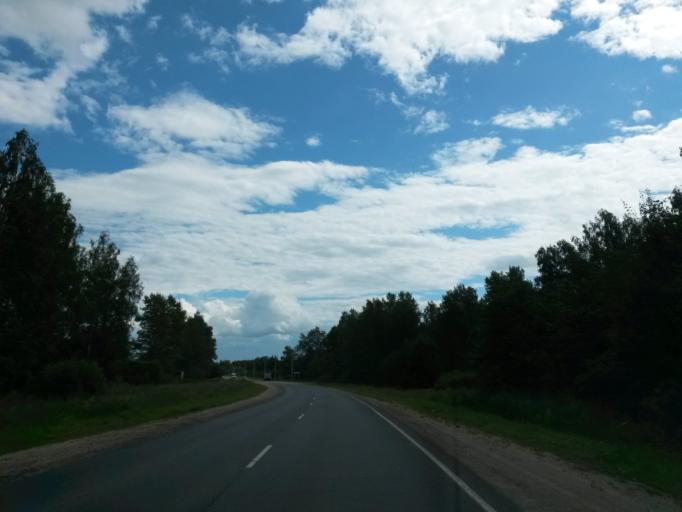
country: RU
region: Ivanovo
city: Novo-Talitsy
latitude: 57.0697
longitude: 40.6924
